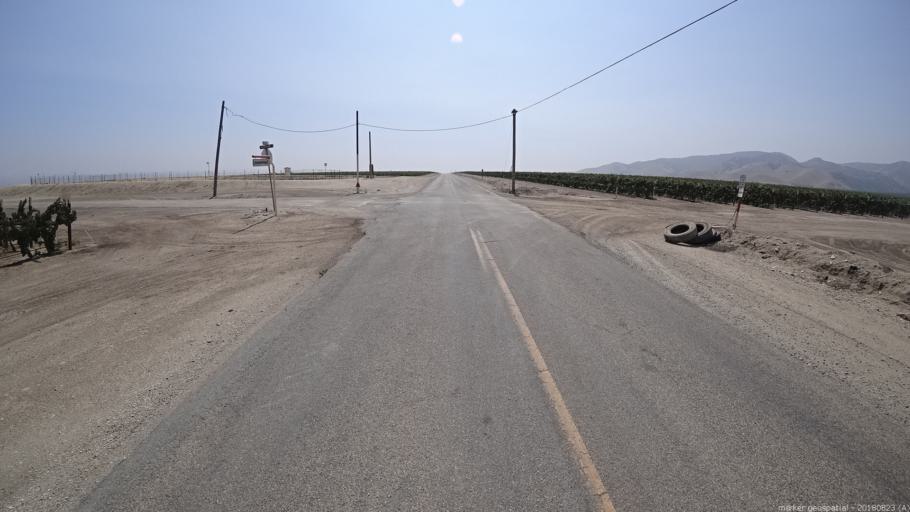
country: US
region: California
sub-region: Monterey County
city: Greenfield
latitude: 36.2731
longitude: -121.2223
